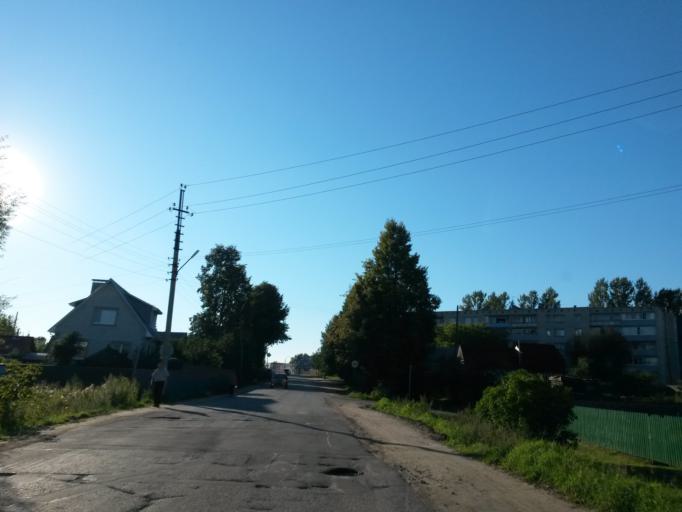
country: RU
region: Jaroslavl
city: Gavrilov-Yam
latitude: 57.2983
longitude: 39.8683
